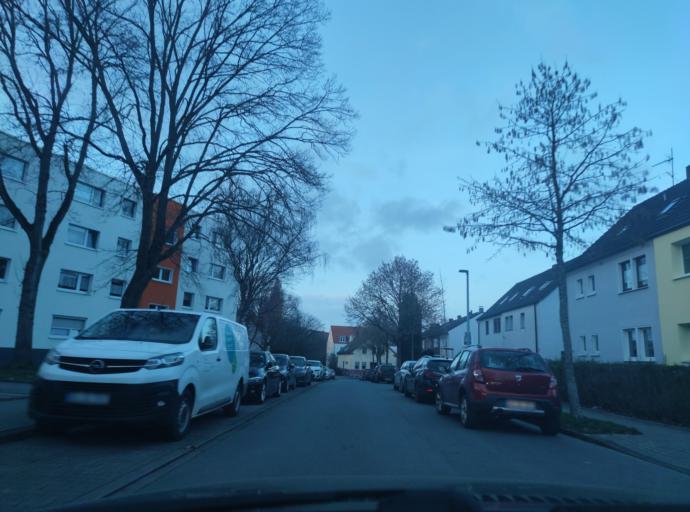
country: DE
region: North Rhine-Westphalia
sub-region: Regierungsbezirk Munster
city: Gelsenkirchen
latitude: 51.4940
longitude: 7.0918
